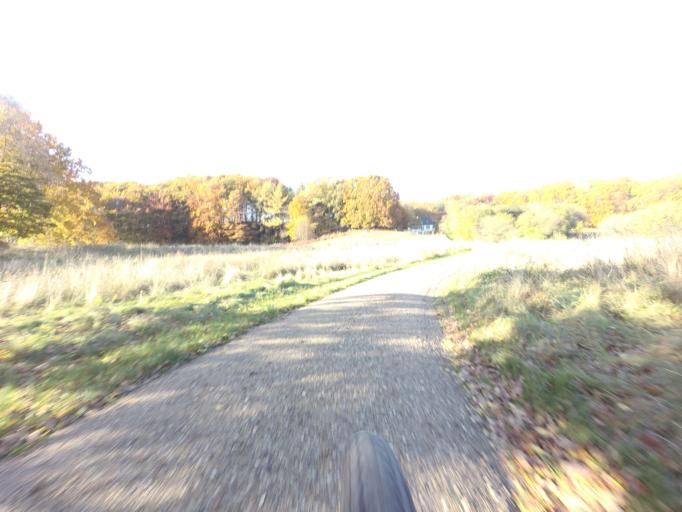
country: DK
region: Central Jutland
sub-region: Syddjurs Kommune
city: Ryomgard
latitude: 56.4481
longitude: 10.6190
